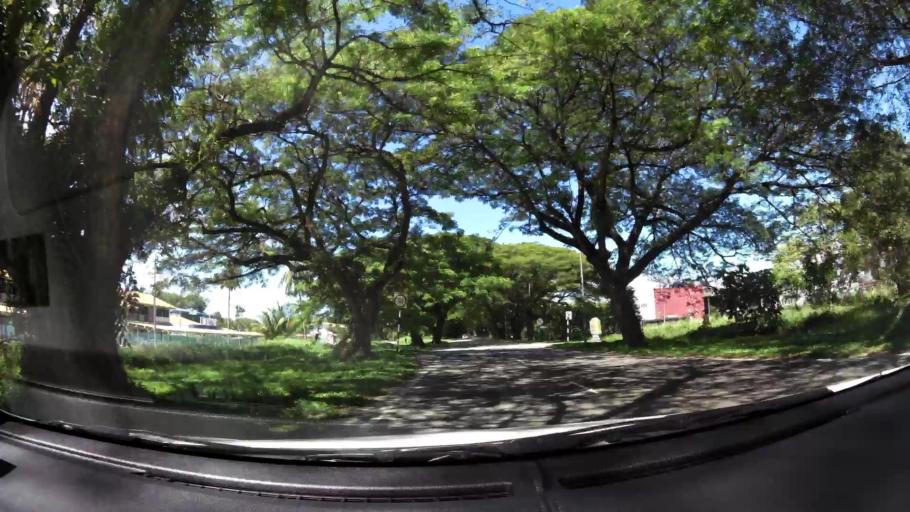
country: BN
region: Brunei and Muara
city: Bandar Seri Begawan
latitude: 5.0293
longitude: 115.0655
